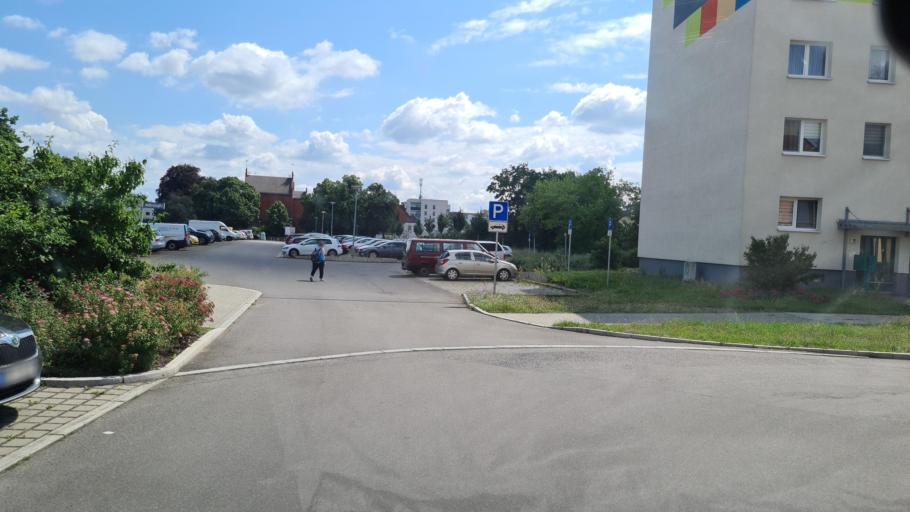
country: DE
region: Brandenburg
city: Senftenberg
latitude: 51.5188
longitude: 14.0011
